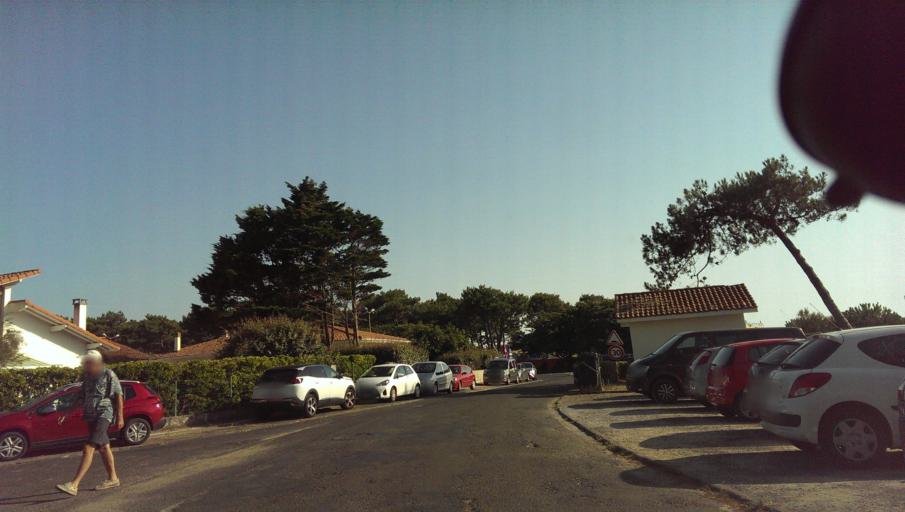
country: FR
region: Aquitaine
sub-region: Departement des Landes
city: Mimizan
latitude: 44.2134
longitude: -1.2911
